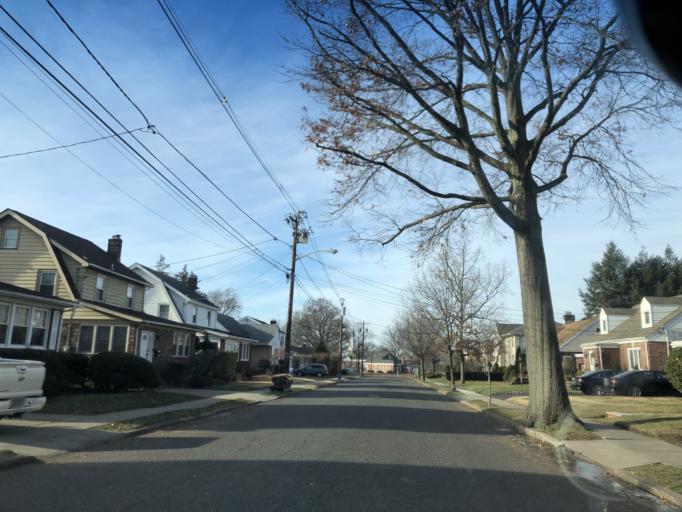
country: US
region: New Jersey
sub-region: Bergen County
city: Fair Lawn
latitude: 40.9284
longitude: -74.1261
